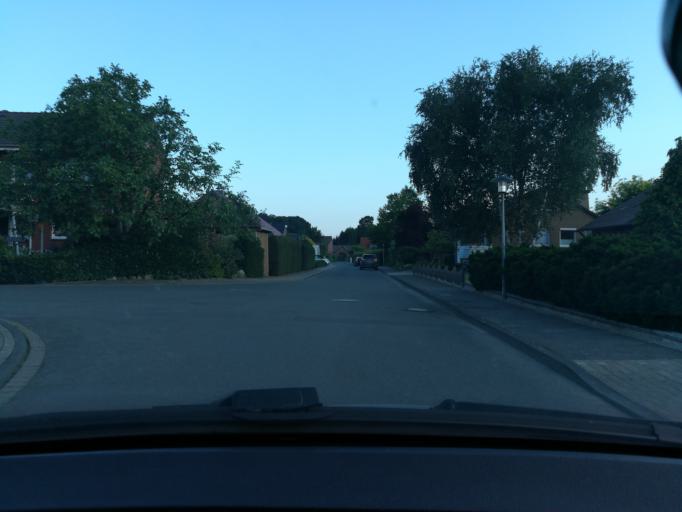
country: DE
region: North Rhine-Westphalia
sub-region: Regierungsbezirk Munster
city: Lienen
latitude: 52.1431
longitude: 7.9758
